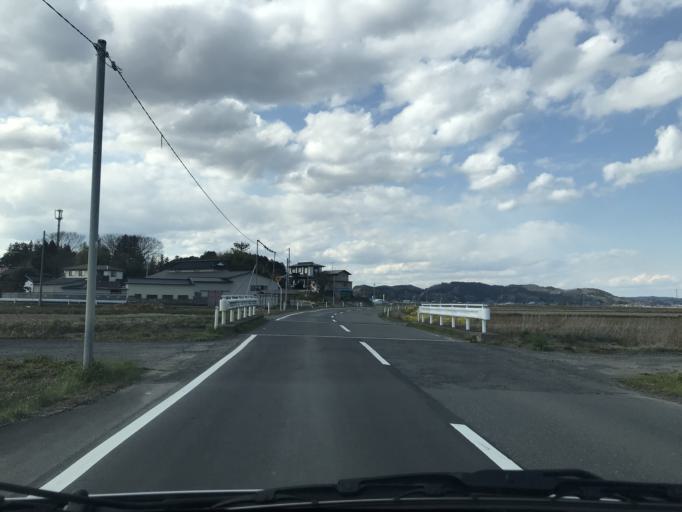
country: JP
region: Miyagi
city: Wakuya
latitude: 38.7249
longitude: 141.2333
